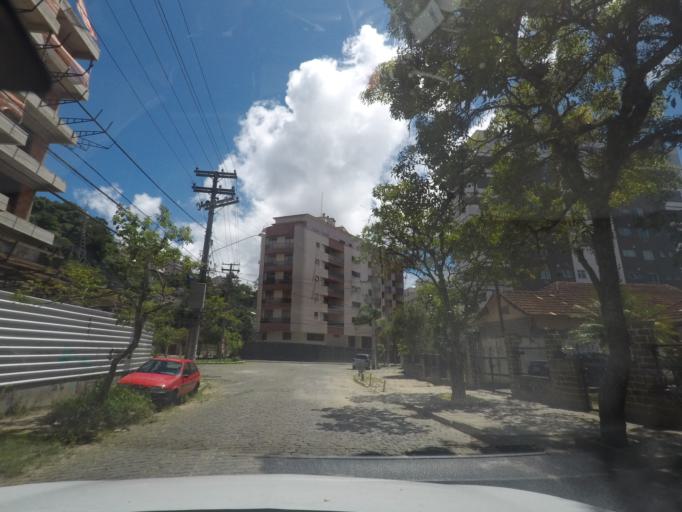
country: BR
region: Rio de Janeiro
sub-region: Teresopolis
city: Teresopolis
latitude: -22.4211
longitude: -42.9798
